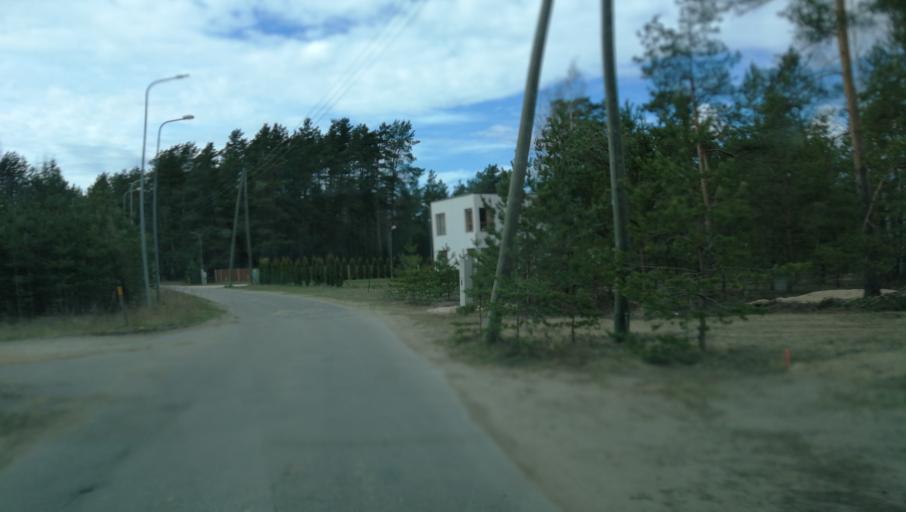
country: LV
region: Garkalne
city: Garkalne
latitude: 57.0409
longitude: 24.4360
